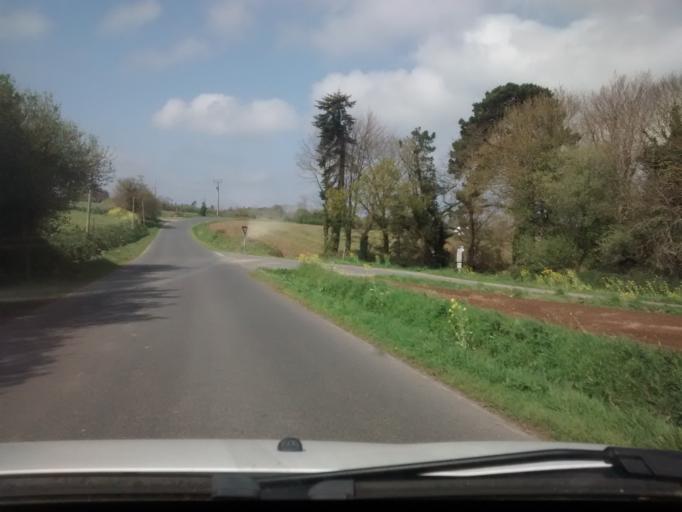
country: FR
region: Brittany
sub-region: Departement des Cotes-d'Armor
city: Trevou-Treguignec
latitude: 48.7894
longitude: -3.3377
